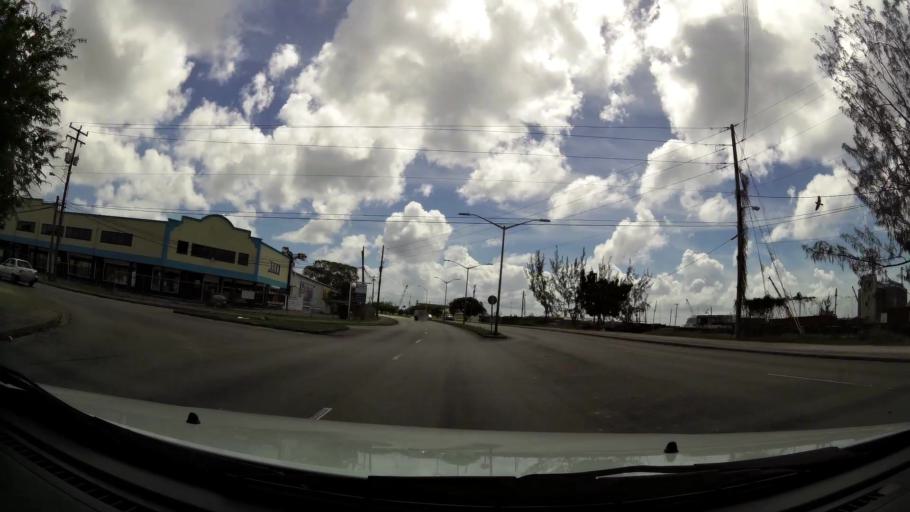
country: BB
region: Saint Michael
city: Bridgetown
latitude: 13.1120
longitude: -59.6269
